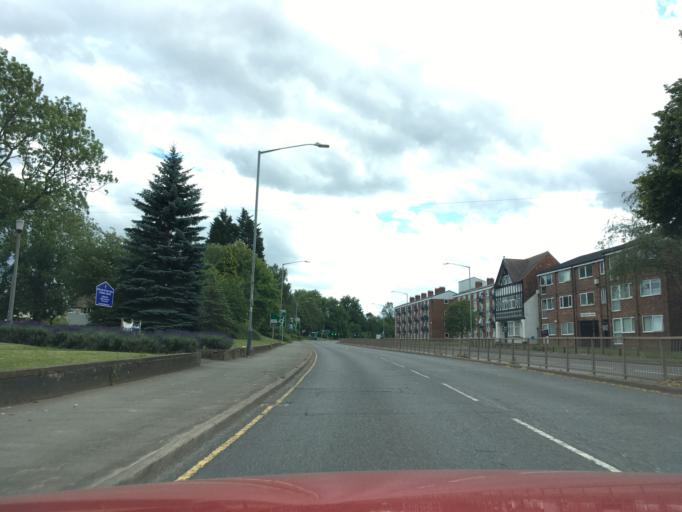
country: GB
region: England
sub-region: Warwickshire
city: Nuneaton
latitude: 52.5175
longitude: -1.4671
